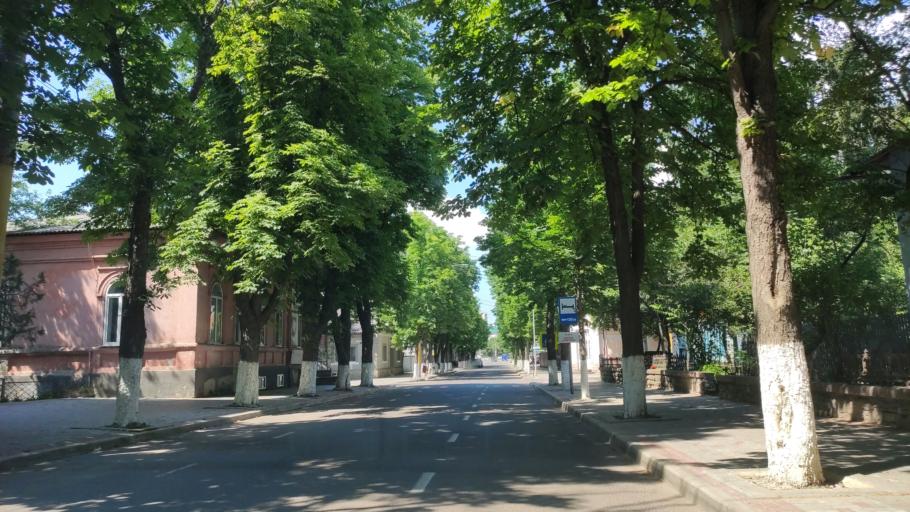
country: MD
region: Raionul Soroca
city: Soroca
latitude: 48.1547
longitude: 28.3021
